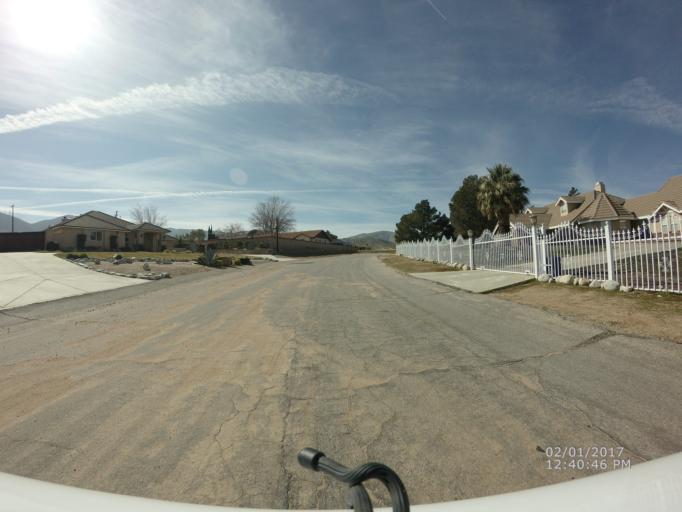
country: US
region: California
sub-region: Los Angeles County
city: Desert View Highlands
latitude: 34.5558
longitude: -118.1490
